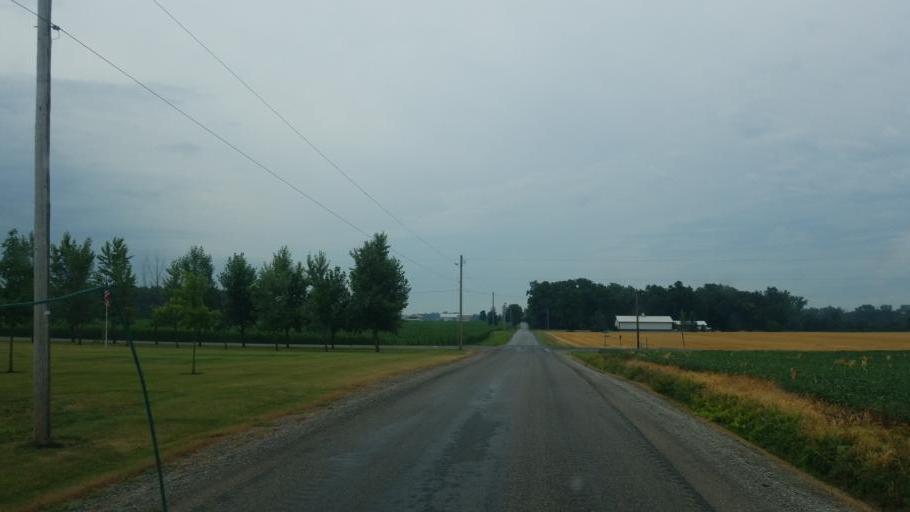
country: US
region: Ohio
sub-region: Williams County
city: Edgerton
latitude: 41.3985
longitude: -84.6701
